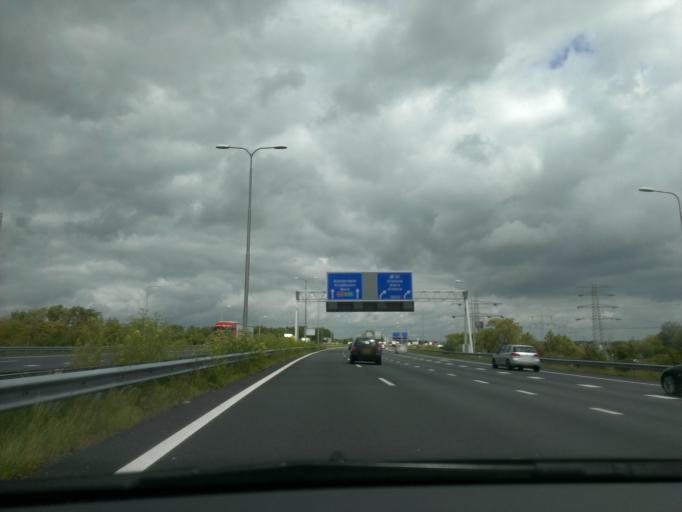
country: NL
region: Limburg
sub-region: Gemeente Stein
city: Urmond
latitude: 50.9805
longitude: 5.7836
